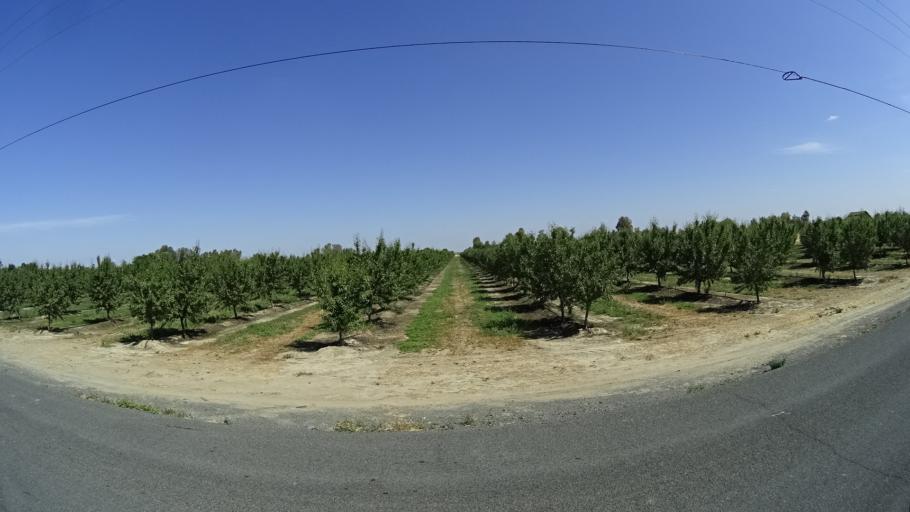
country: US
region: California
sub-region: Kings County
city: Lemoore
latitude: 36.2692
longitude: -119.7591
